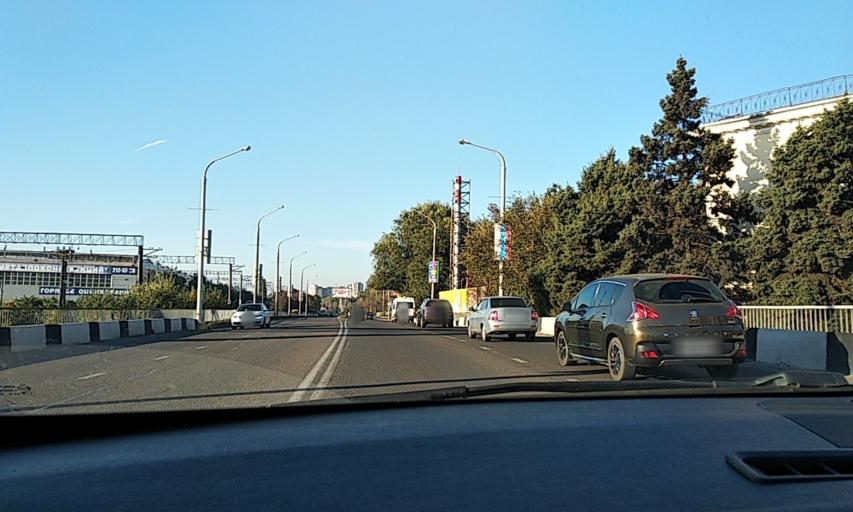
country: RU
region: Krasnodarskiy
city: Krasnodar
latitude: 45.0133
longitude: 38.9753
